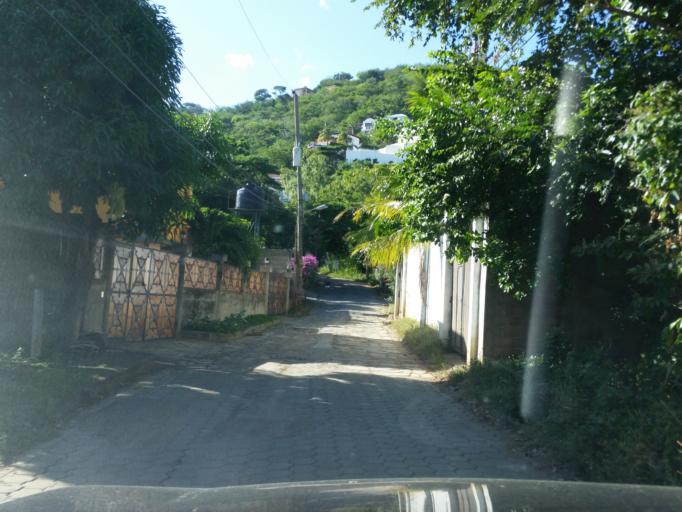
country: NI
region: Rivas
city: San Juan del Sur
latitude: 11.2626
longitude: -85.8779
